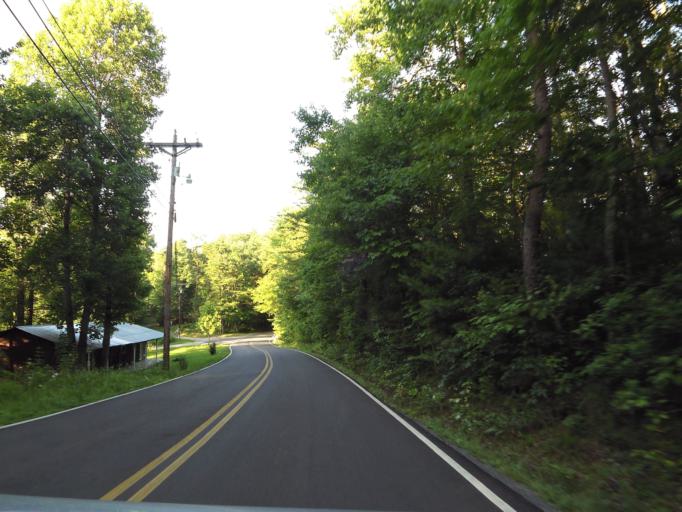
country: US
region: Tennessee
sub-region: Blount County
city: Maryville
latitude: 35.6416
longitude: -83.9189
